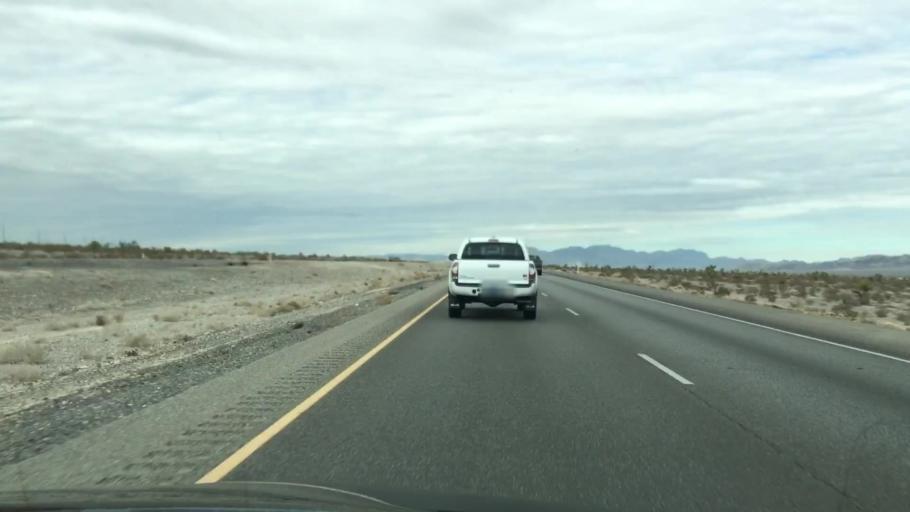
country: US
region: Nevada
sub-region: Clark County
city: Summerlin South
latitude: 36.4545
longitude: -115.4402
